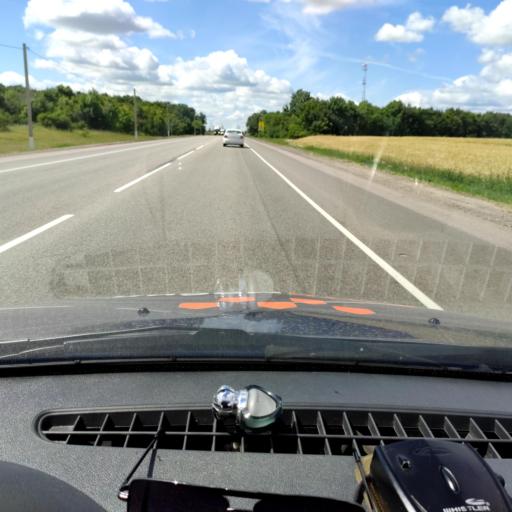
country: RU
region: Lipetsk
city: Borinskoye
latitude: 52.4665
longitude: 39.3398
